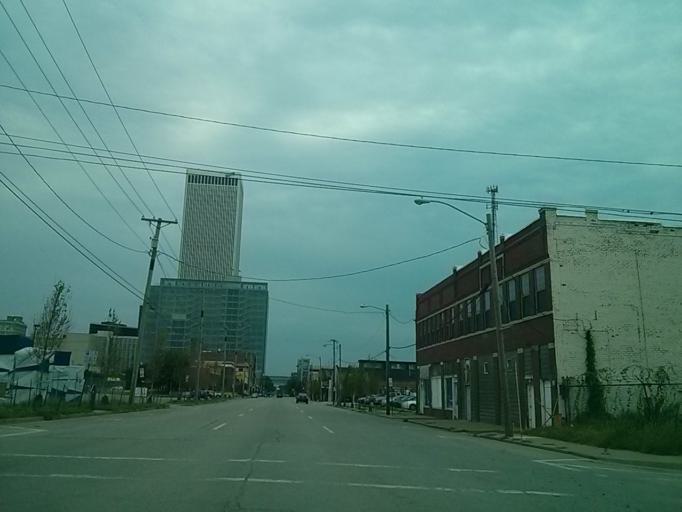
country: US
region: Oklahoma
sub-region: Tulsa County
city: Tulsa
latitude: 36.1578
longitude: -95.9850
